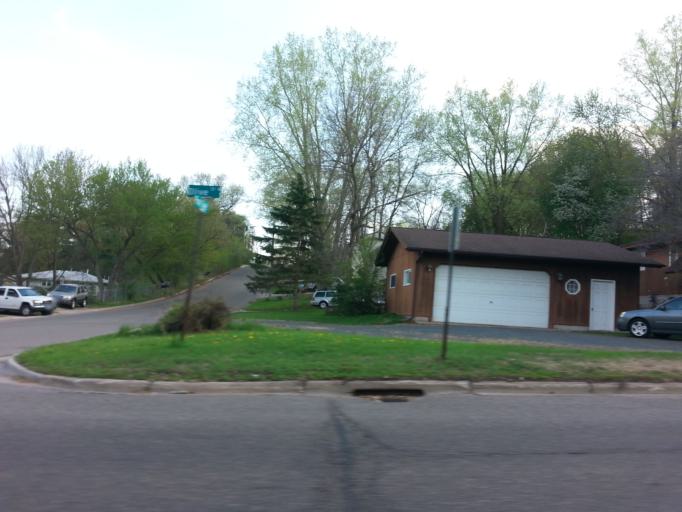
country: US
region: Minnesota
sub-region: Washington County
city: Stillwater
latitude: 45.0531
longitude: -92.8298
